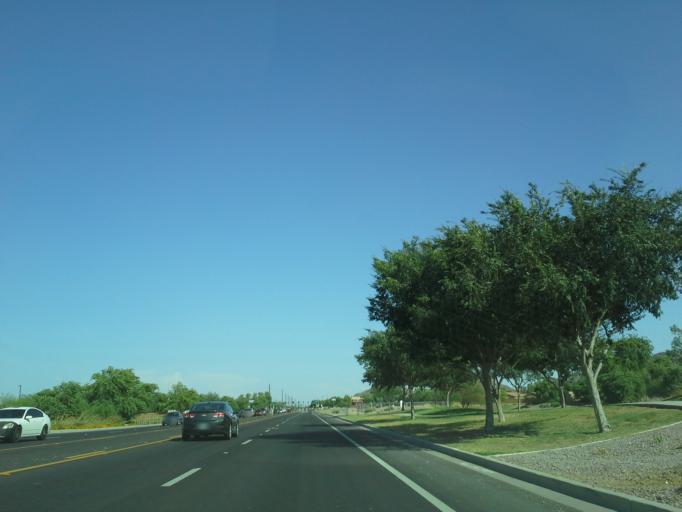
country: US
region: Arizona
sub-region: Pinal County
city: San Tan Valley
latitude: 33.1830
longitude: -111.5894
